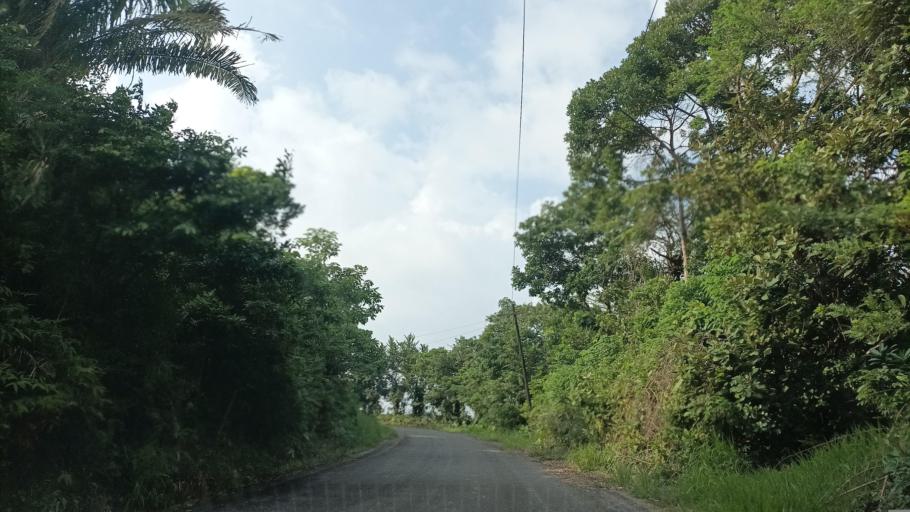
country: MX
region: Veracruz
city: Allende
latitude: 18.1305
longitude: -94.2859
